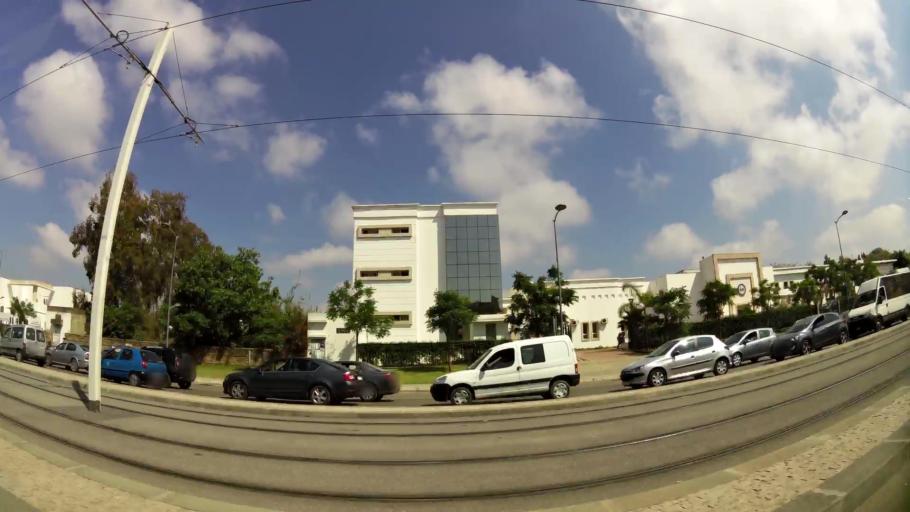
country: MA
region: Rabat-Sale-Zemmour-Zaer
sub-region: Rabat
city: Rabat
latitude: 33.9886
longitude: -6.8587
